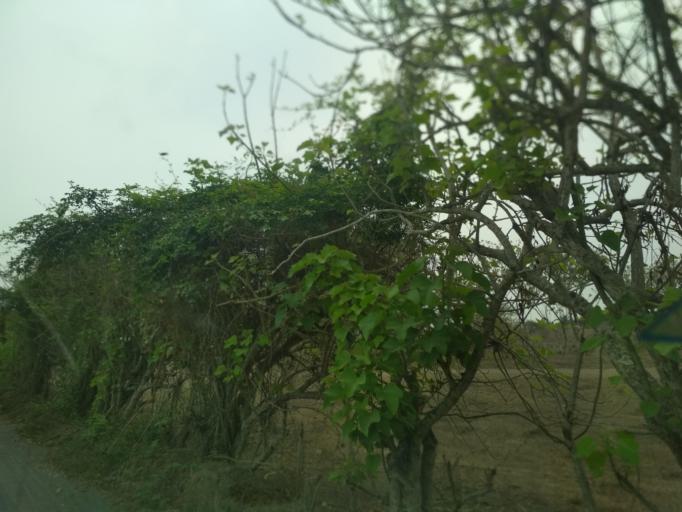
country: MX
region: Veracruz
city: Paso del Toro
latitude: 19.0296
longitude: -96.1485
